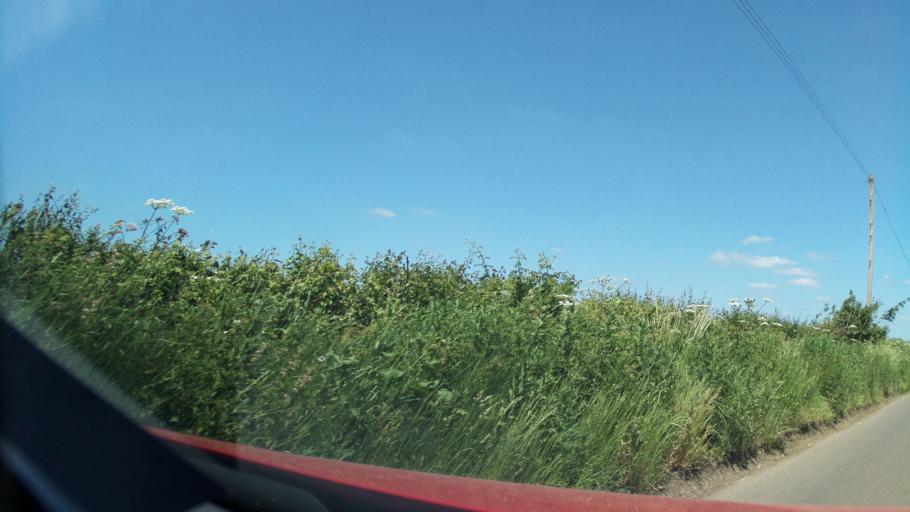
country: GB
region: England
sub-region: Wiltshire
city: Lyneham
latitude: 51.4848
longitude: -1.9427
